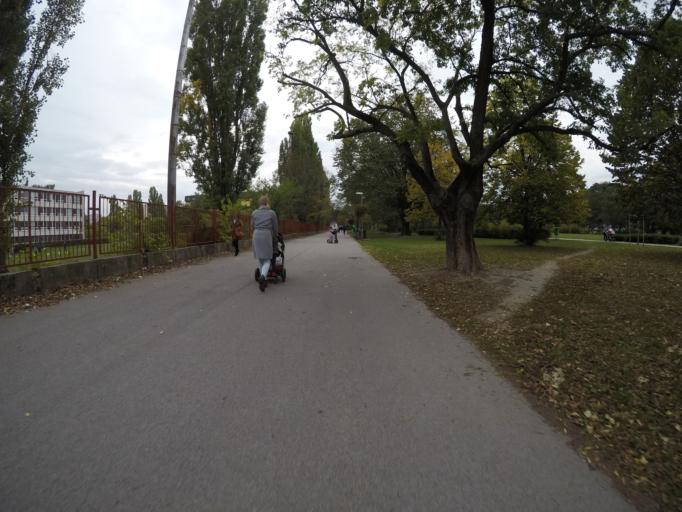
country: SK
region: Bratislavsky
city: Bratislava
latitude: 48.1612
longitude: 17.1702
